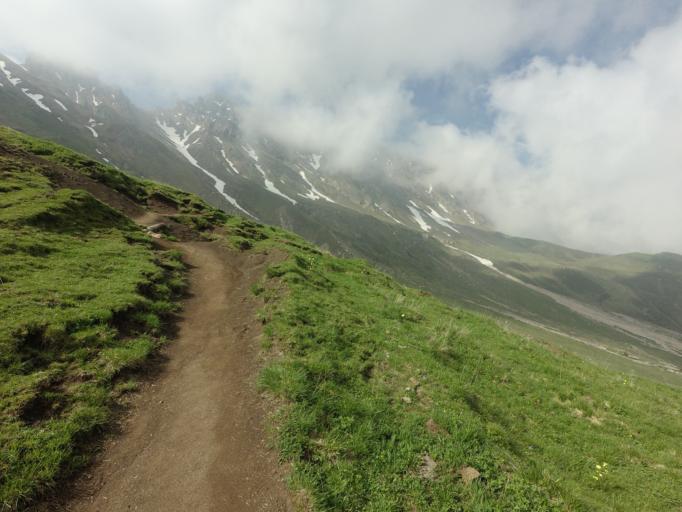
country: IT
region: Trentino-Alto Adige
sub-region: Bolzano
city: Ortisei
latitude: 46.5091
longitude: 11.6347
